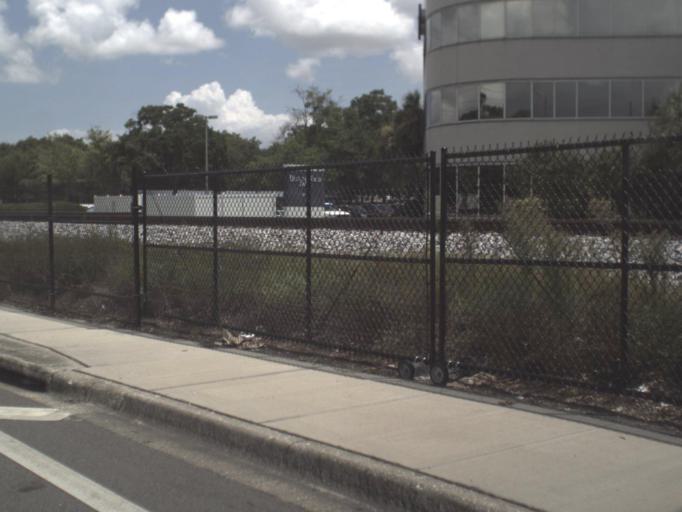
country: US
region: Florida
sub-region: Hillsborough County
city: Carrollwood
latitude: 28.0362
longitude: -82.4998
